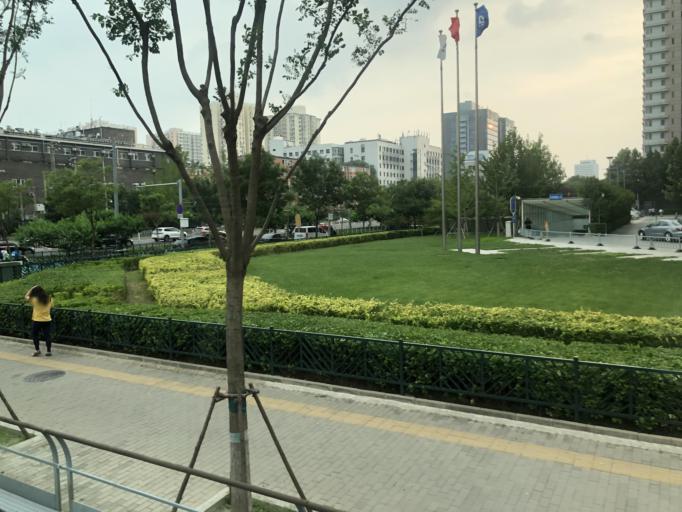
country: CN
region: Beijing
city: Jinrongjie
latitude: 39.9315
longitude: 116.3191
